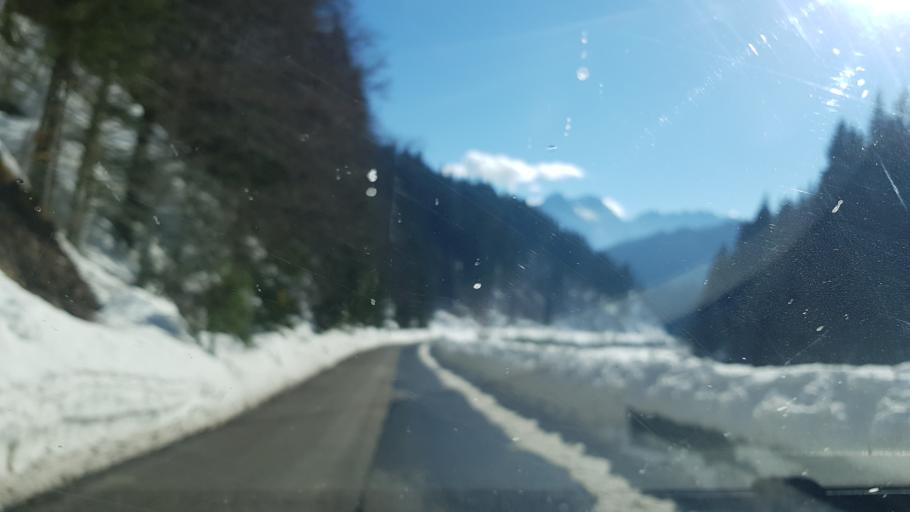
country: IT
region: Friuli Venezia Giulia
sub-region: Provincia di Udine
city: Malborghetto
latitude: 46.5381
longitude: 13.4740
